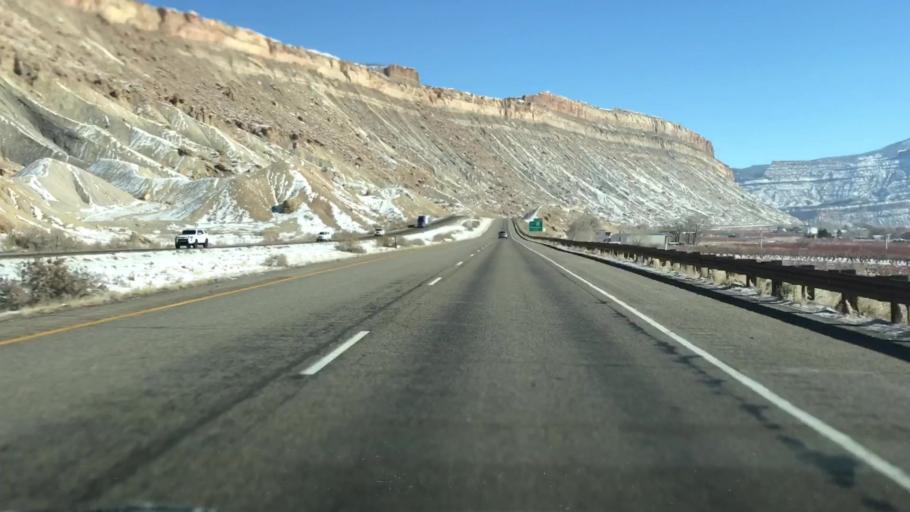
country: US
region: Colorado
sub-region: Mesa County
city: Palisade
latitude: 39.1185
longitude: -108.3846
